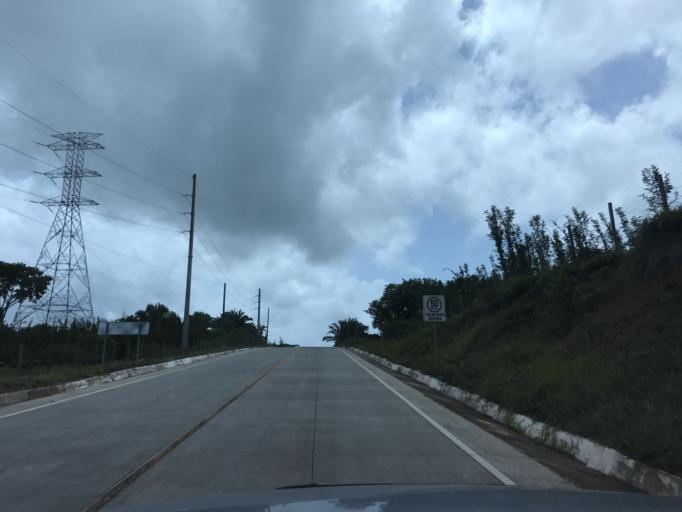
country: GT
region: Izabal
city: Morales
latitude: 15.6240
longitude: -89.0621
